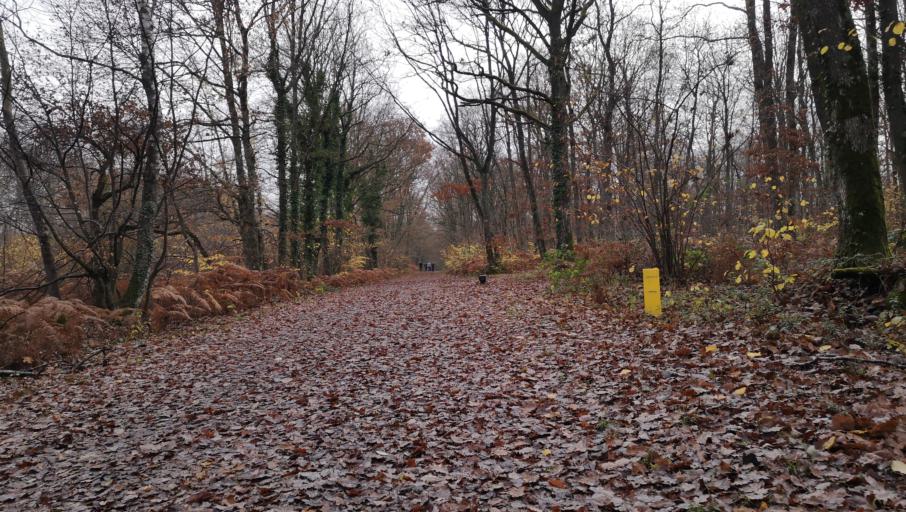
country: FR
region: Centre
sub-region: Departement du Loiret
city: Chanteau
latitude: 47.9440
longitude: 1.9860
